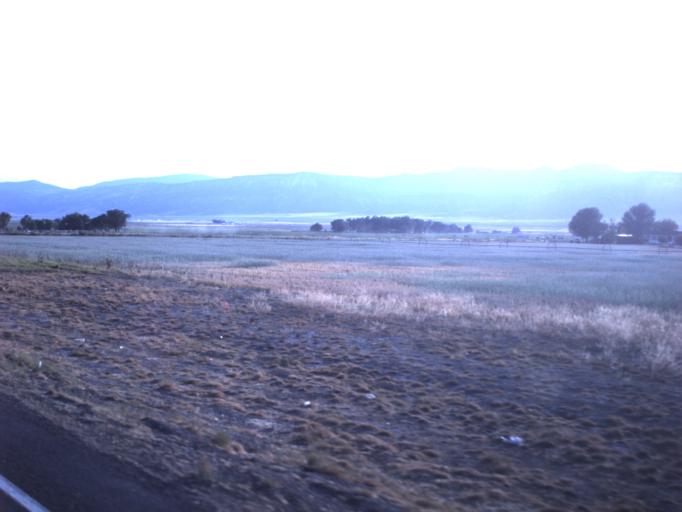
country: US
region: Utah
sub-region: Sanpete County
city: Ephraim
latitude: 39.3933
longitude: -111.5774
